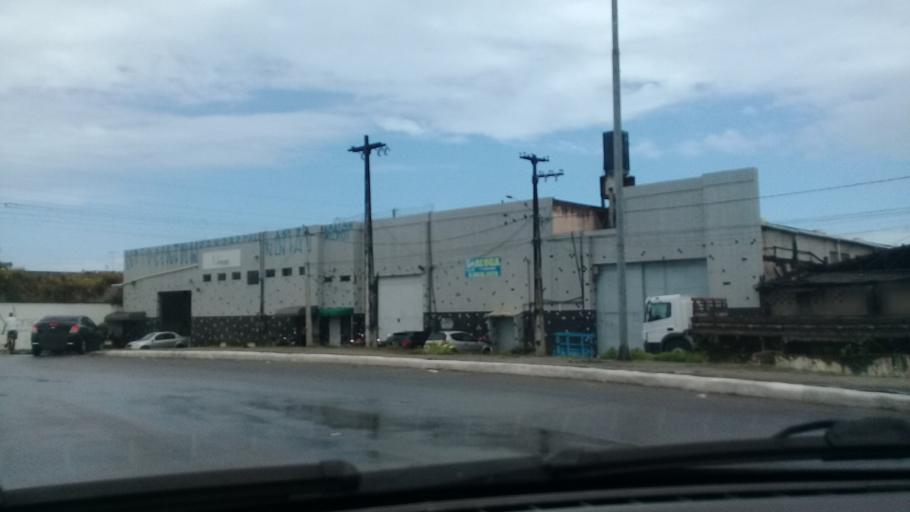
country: BR
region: Pernambuco
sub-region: Jaboatao Dos Guararapes
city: Jaboatao
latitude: -8.1438
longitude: -34.9176
